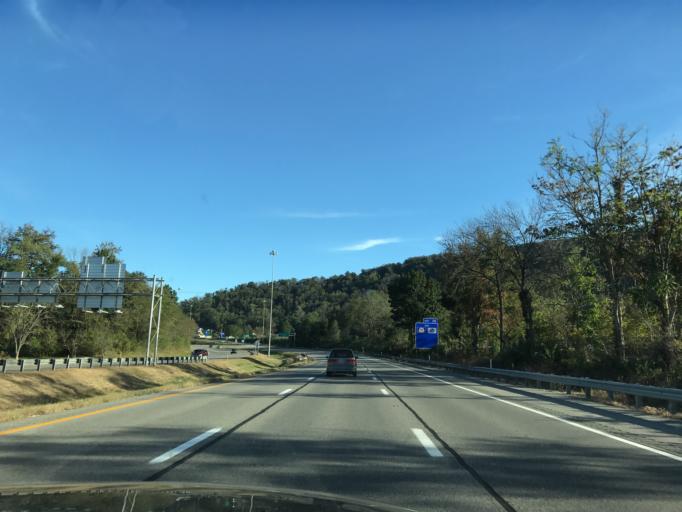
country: US
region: West Virginia
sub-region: Ohio County
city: Wheeling
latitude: 40.0700
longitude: -80.6981
